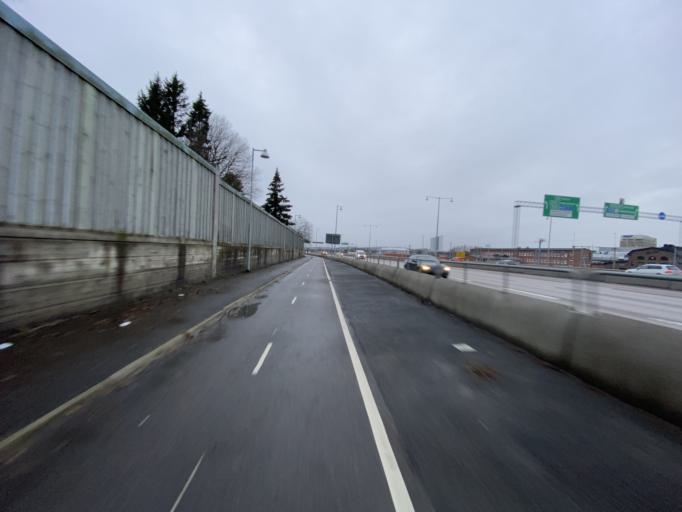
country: SE
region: Vaestra Goetaland
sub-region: Goteborg
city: Eriksbo
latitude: 57.7242
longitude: 12.0185
